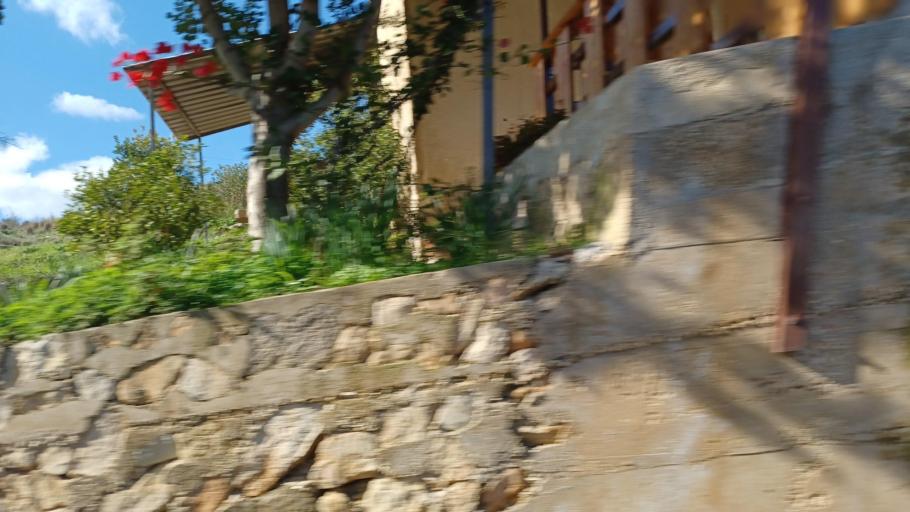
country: CY
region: Pafos
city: Polis
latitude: 34.9644
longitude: 32.4223
